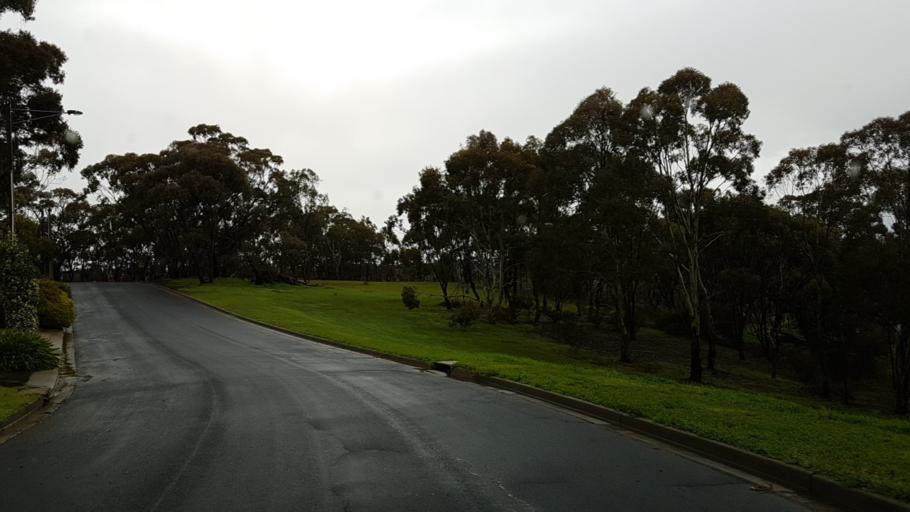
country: AU
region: South Australia
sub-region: Onkaparinga
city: Bedford Park
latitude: -35.0441
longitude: 138.5778
